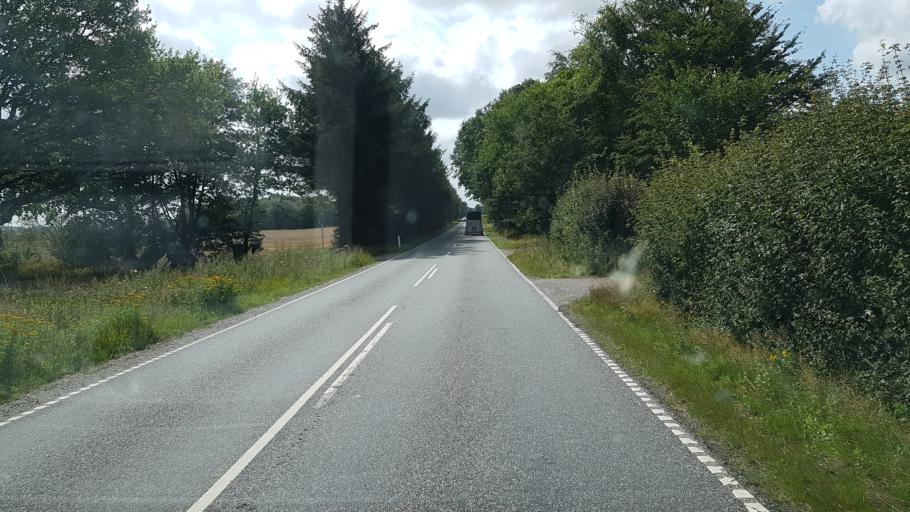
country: DK
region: South Denmark
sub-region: Vejen Kommune
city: Brorup
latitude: 55.5289
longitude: 9.0450
